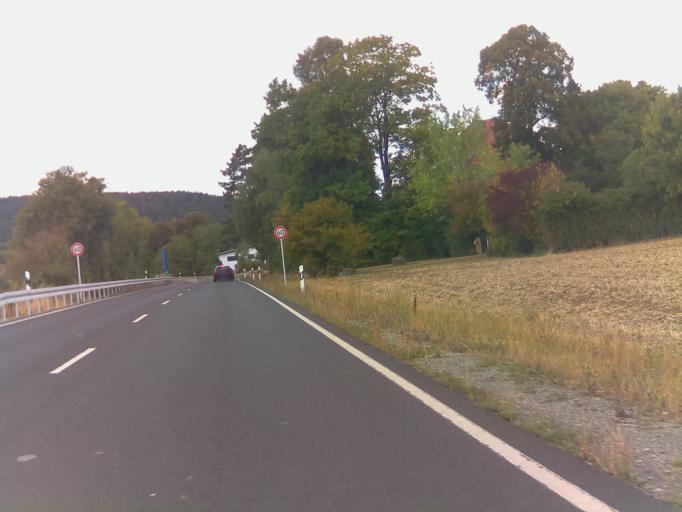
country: DE
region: Bavaria
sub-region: Regierungsbezirk Unterfranken
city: Stockheim
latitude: 50.4495
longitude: 10.2871
